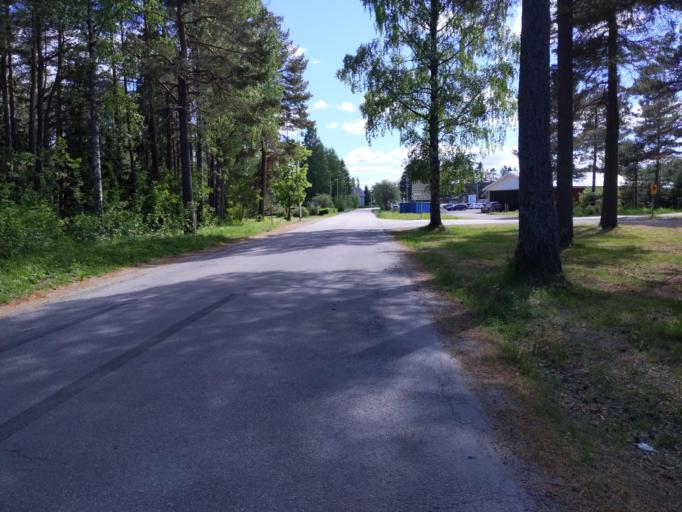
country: SE
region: Vaesternorrland
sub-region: OErnskoeldsviks Kommun
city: Kopmanholmen
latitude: 63.1726
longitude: 18.5675
